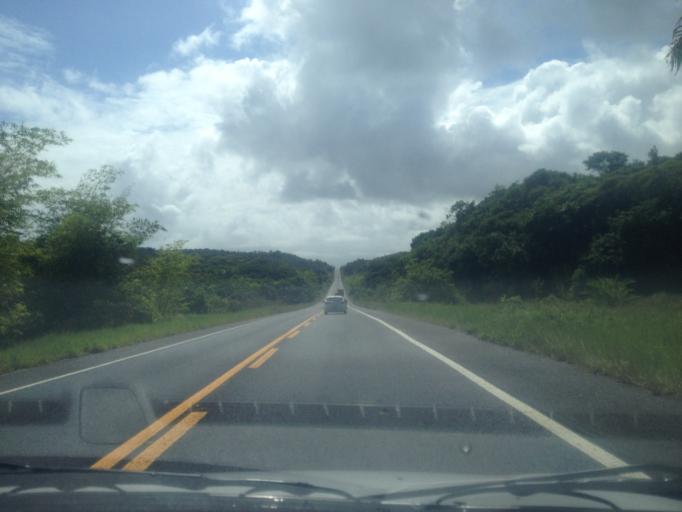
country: BR
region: Sergipe
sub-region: Indiaroba
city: Indiaroba
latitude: -11.5994
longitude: -37.5412
